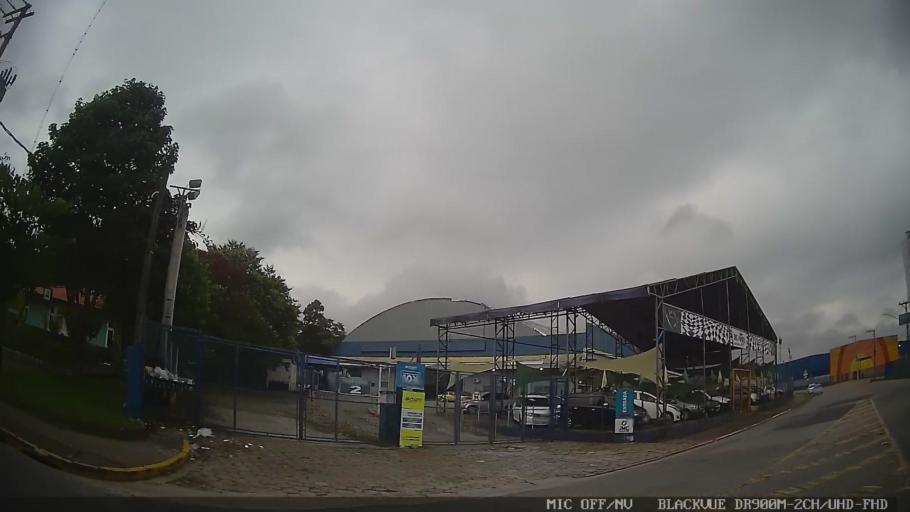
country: BR
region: Sao Paulo
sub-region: Mogi das Cruzes
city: Mogi das Cruzes
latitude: -23.5128
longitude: -46.1970
